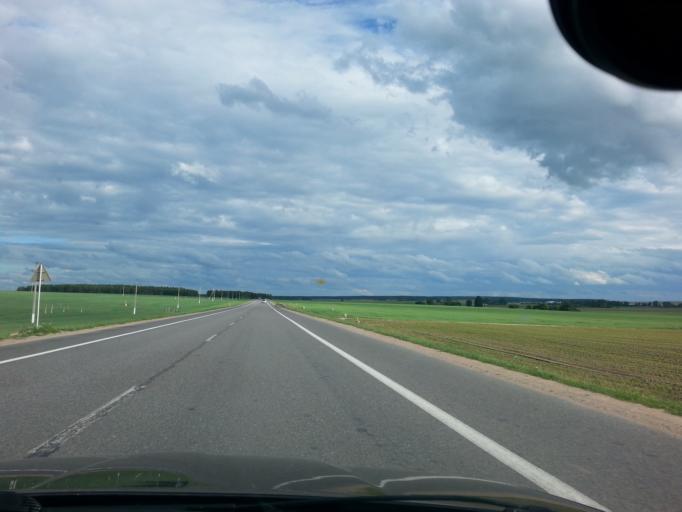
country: BY
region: Grodnenskaya
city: Astravyets
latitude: 54.7516
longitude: 26.0780
